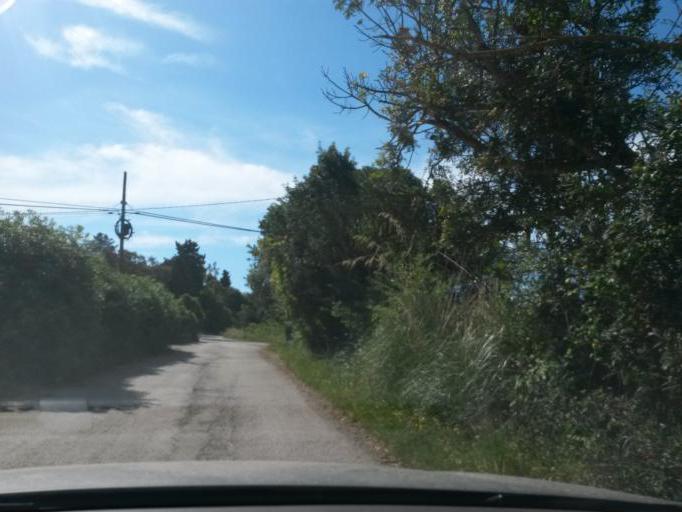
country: IT
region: Tuscany
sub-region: Provincia di Livorno
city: Rio nell'Elba
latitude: 42.8072
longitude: 10.4093
